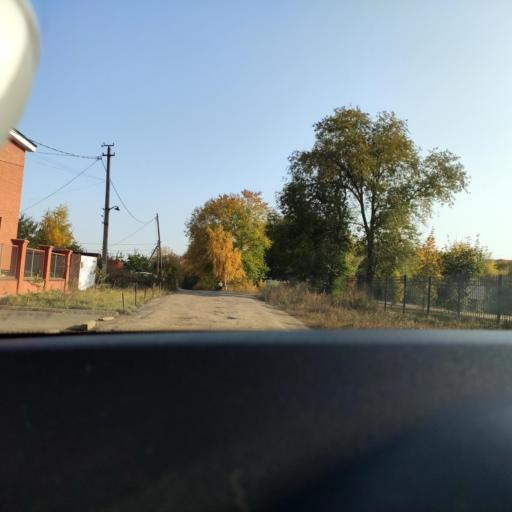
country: RU
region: Samara
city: Samara
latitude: 53.2175
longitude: 50.2141
